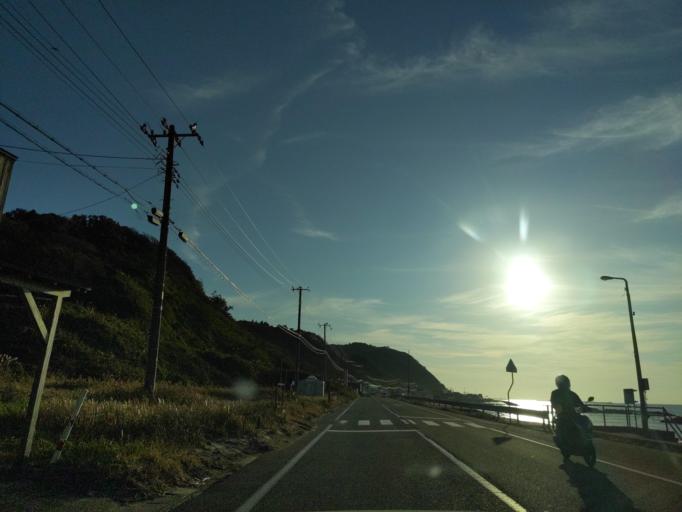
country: JP
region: Niigata
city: Nagaoka
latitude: 37.5565
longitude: 138.7110
